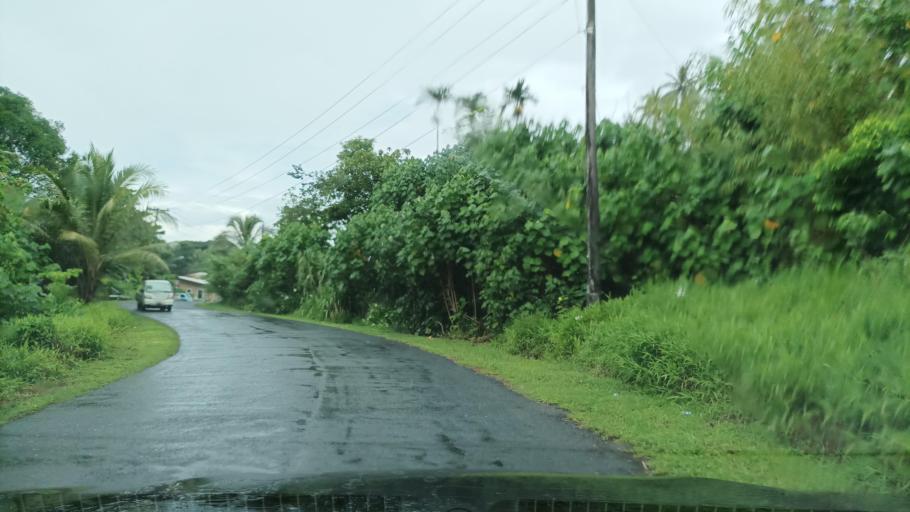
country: FM
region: Pohnpei
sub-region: Kolonia Municipality
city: Kolonia
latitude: 6.9628
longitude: 158.2499
